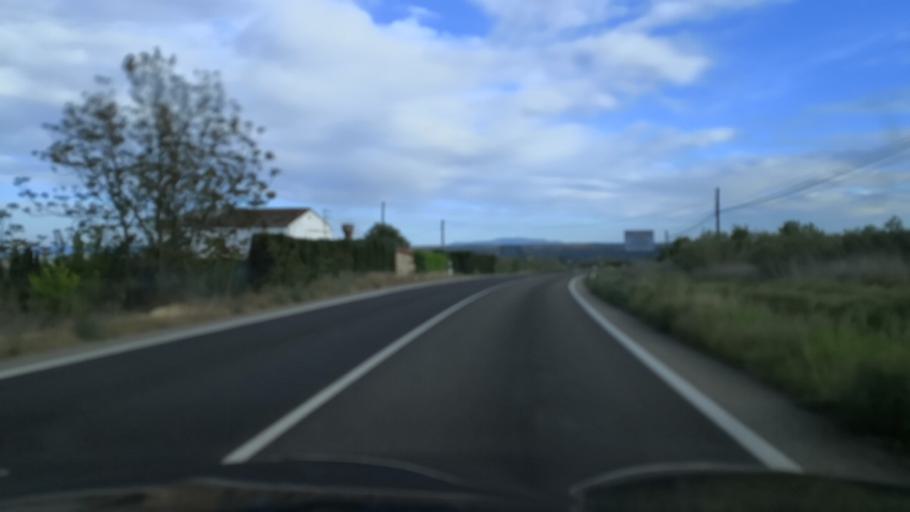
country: ES
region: Extremadura
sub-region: Provincia de Caceres
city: Coria
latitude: 40.0025
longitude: -6.5515
